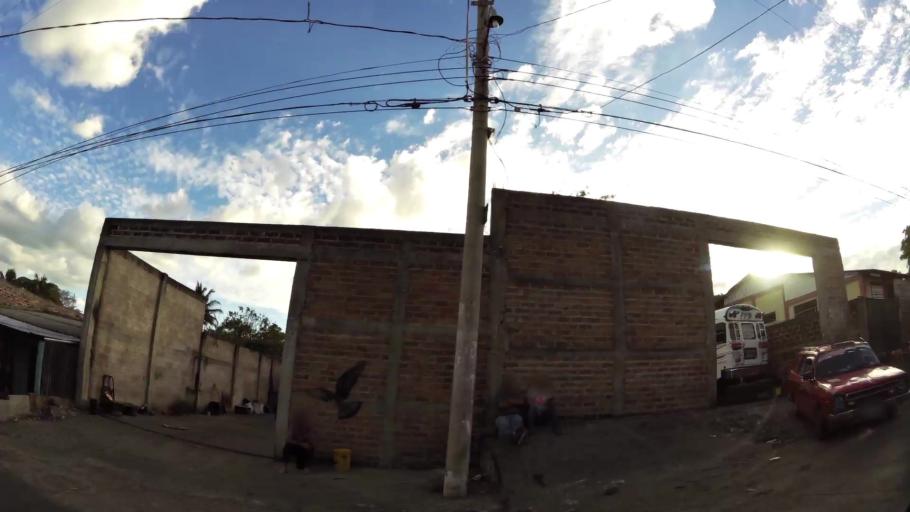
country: SV
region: Cuscatlan
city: Cojutepeque
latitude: 13.7183
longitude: -88.9294
